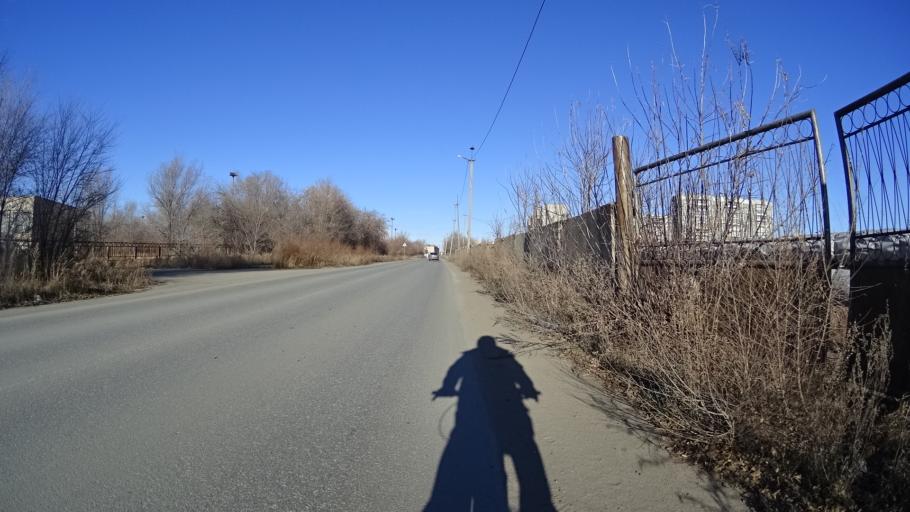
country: RU
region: Chelyabinsk
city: Troitsk
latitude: 54.0445
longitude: 61.6404
